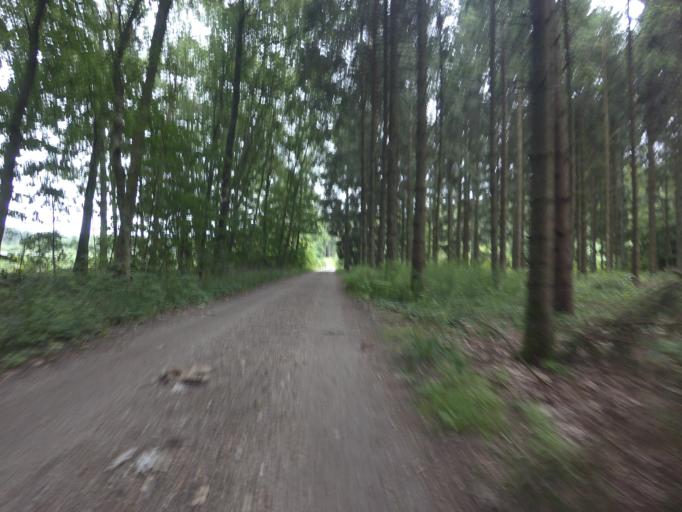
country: DK
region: Central Jutland
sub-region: Silkeborg Kommune
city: Virklund
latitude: 56.0248
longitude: 9.4954
